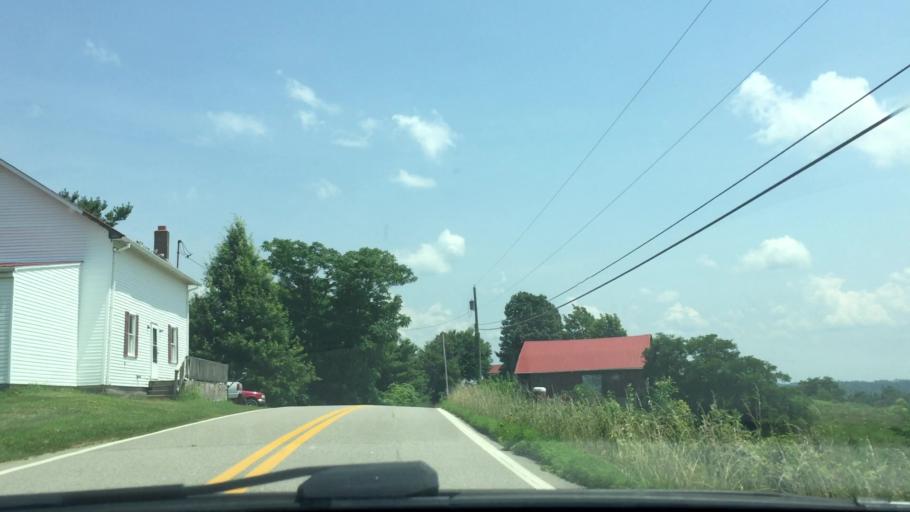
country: US
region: West Virginia
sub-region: Wetzel County
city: New Martinsville
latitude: 39.6987
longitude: -80.7677
